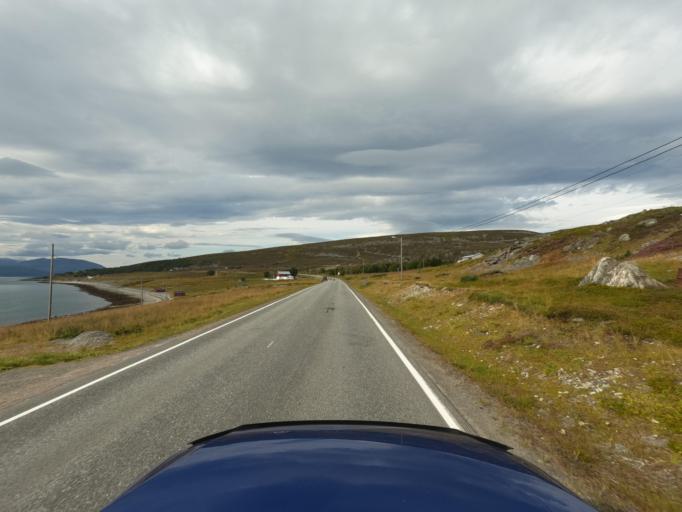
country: NO
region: Finnmark Fylke
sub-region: Kvalsund
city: Kvalsund
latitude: 70.5096
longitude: 23.8591
